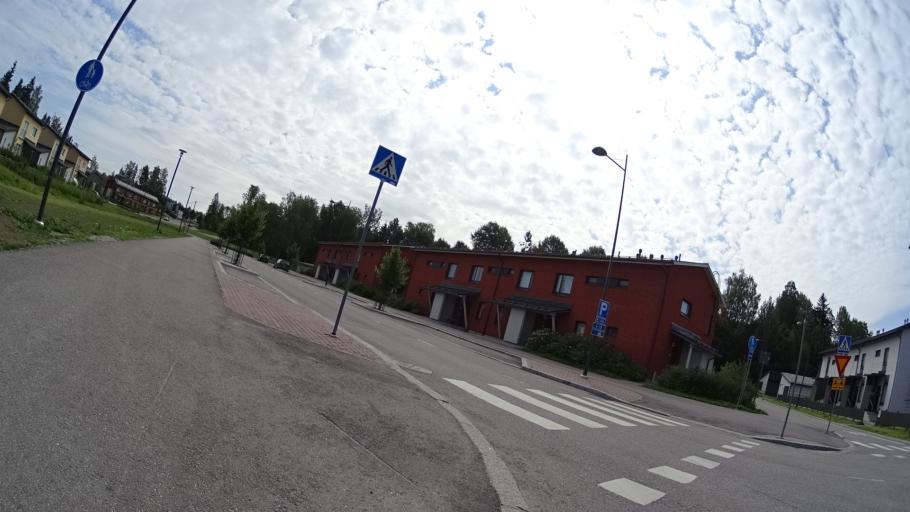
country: FI
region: Uusimaa
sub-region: Helsinki
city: Espoo
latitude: 60.1915
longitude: 24.5896
